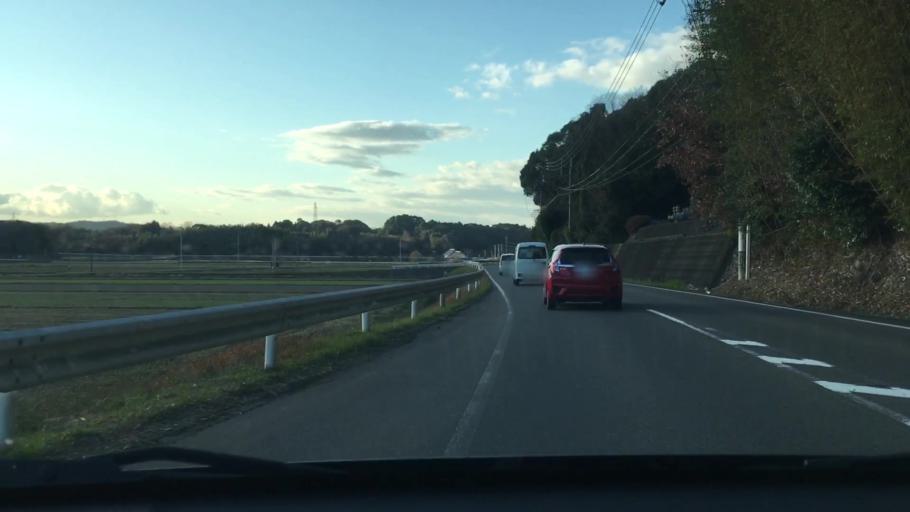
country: JP
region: Oita
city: Bungo-Takada-shi
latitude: 33.5104
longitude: 131.3574
